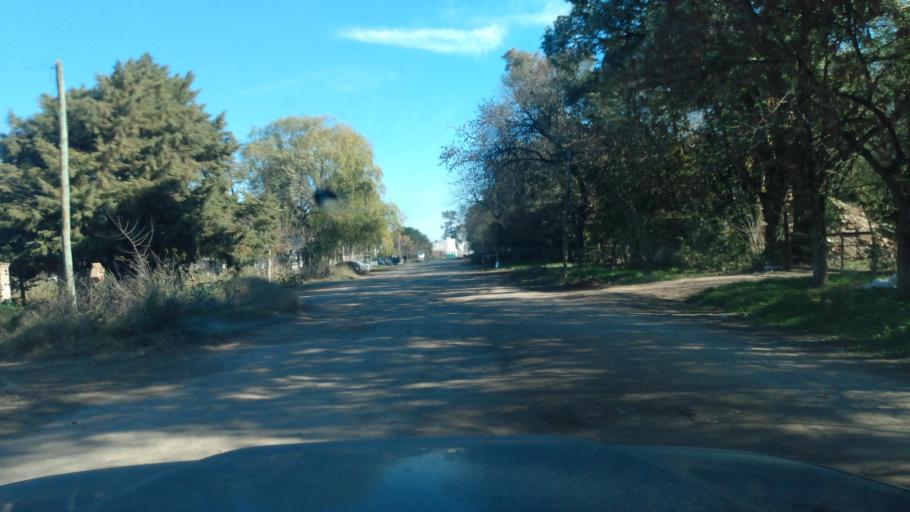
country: AR
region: Buenos Aires
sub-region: Partido de Lujan
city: Lujan
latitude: -34.5768
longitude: -59.0960
